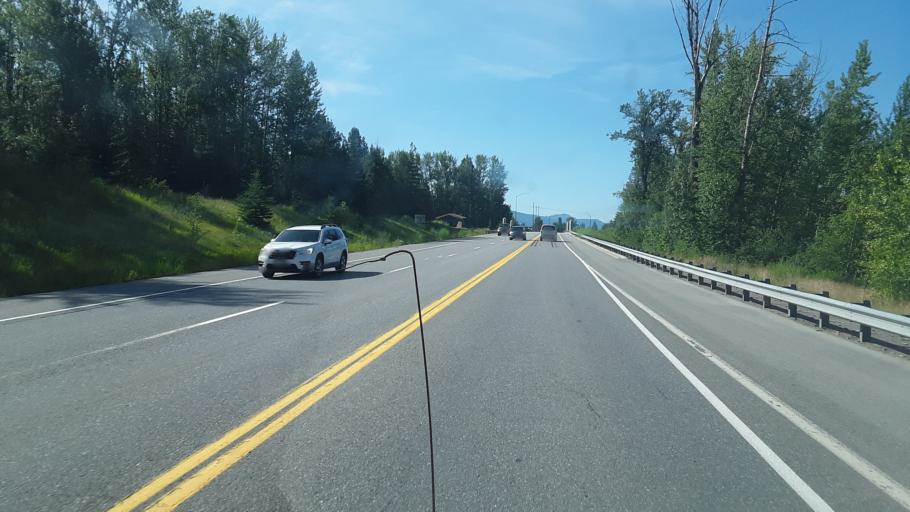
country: US
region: Idaho
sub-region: Bonner County
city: Sandpoint
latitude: 48.2925
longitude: -116.5490
